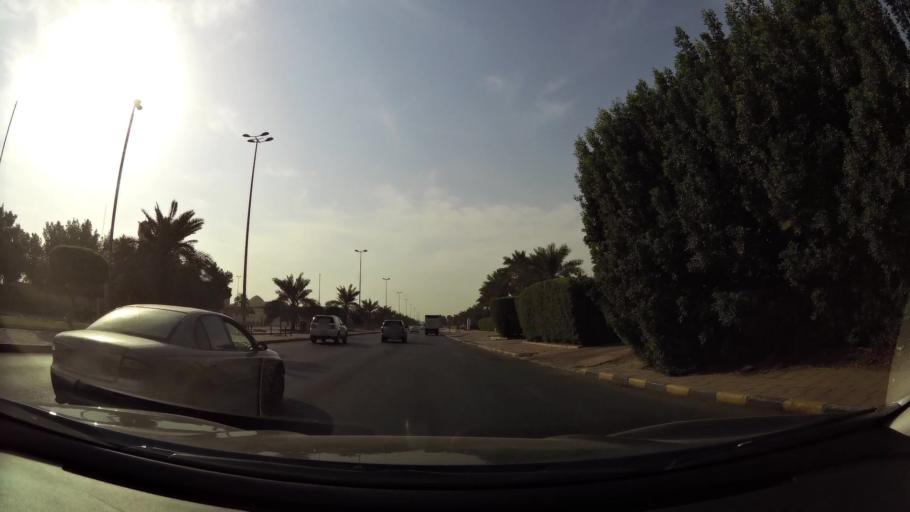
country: KW
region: Muhafazat Hawalli
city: Salwa
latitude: 29.2851
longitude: 48.0866
